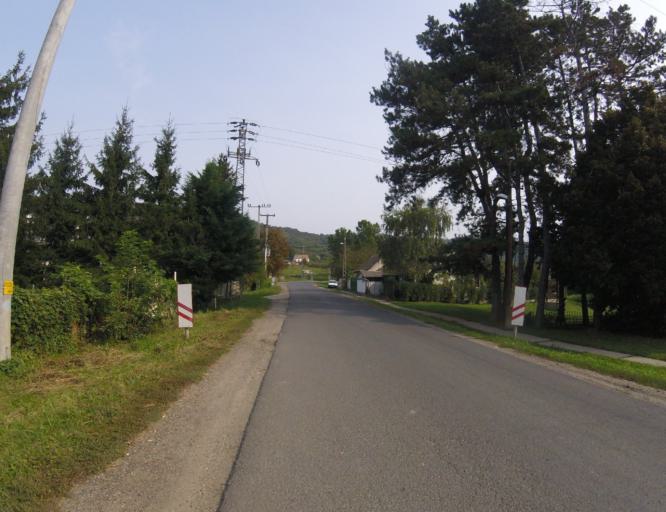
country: HU
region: Pest
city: Veroce
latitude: 47.8293
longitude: 19.0399
